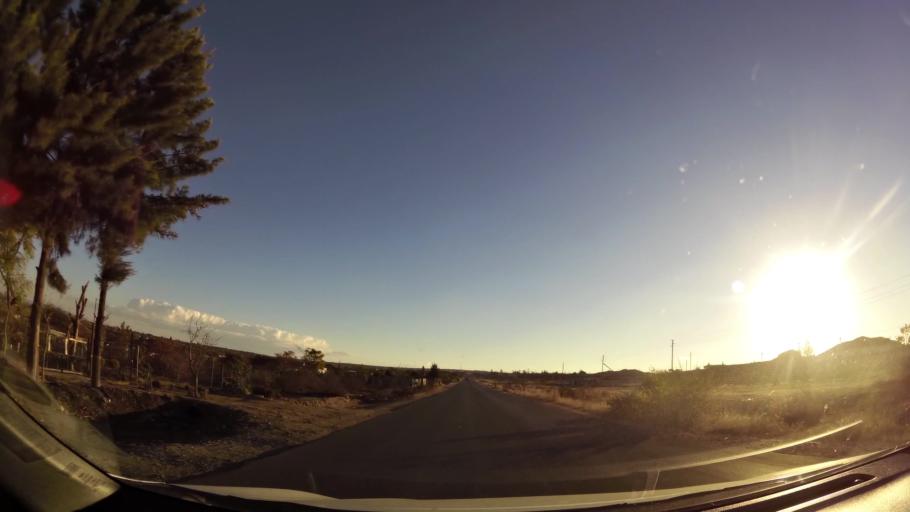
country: ZA
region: Limpopo
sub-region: Capricorn District Municipality
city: Polokwane
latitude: -23.8371
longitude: 29.3573
